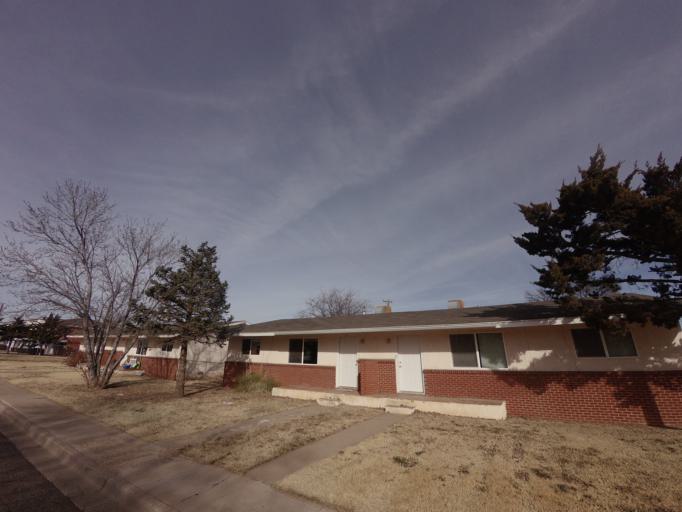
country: US
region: New Mexico
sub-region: Curry County
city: Clovis
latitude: 34.4152
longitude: -103.2165
